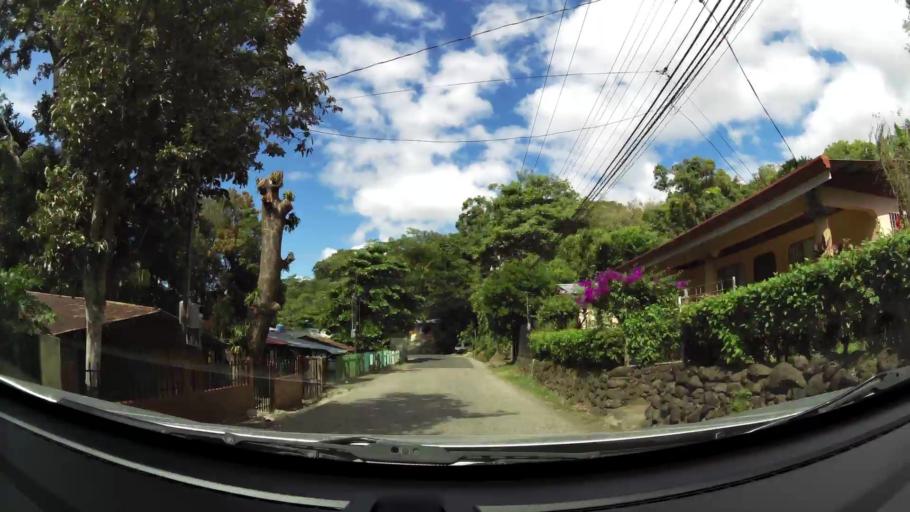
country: CR
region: Guanacaste
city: Juntas
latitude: 10.2820
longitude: -84.9491
